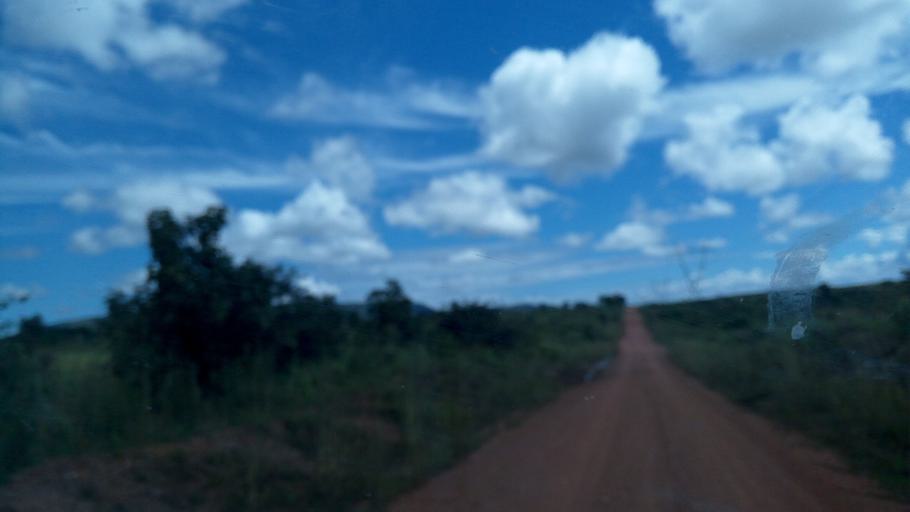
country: CD
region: Katanga
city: Kalemie
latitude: -5.7708
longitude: 29.1063
